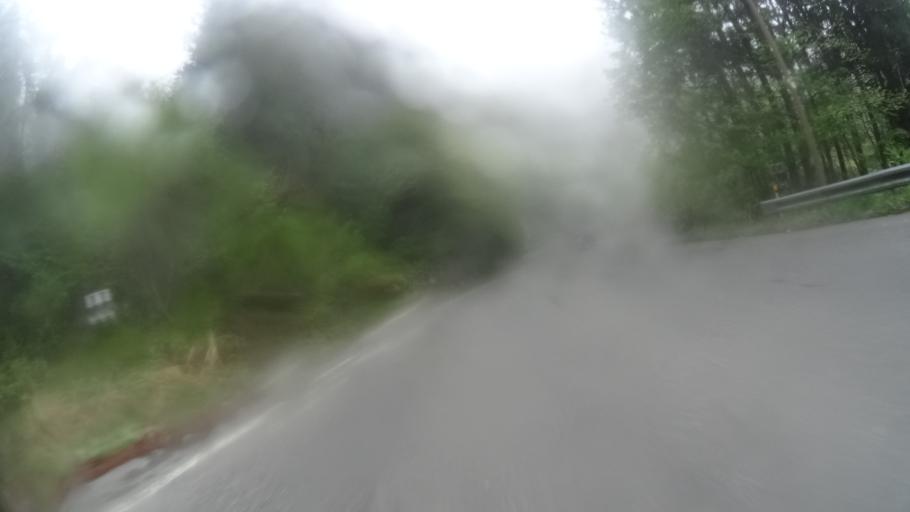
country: JP
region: Nagano
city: Nakano
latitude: 36.7228
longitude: 138.4519
